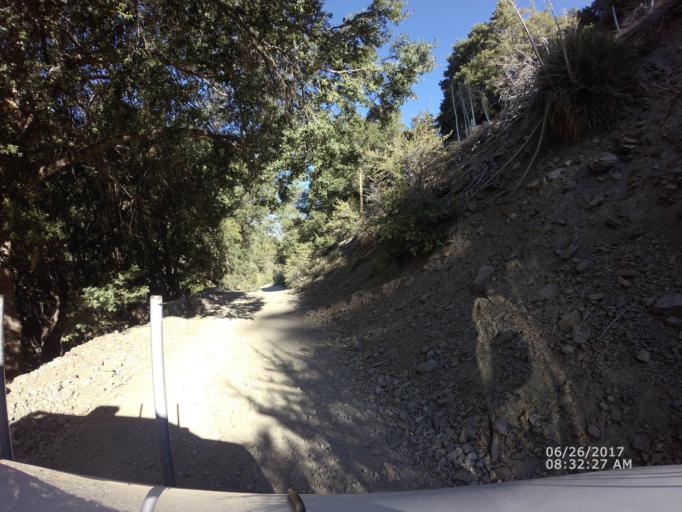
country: US
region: California
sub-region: San Bernardino County
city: Pinon Hills
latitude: 34.3781
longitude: -117.7614
